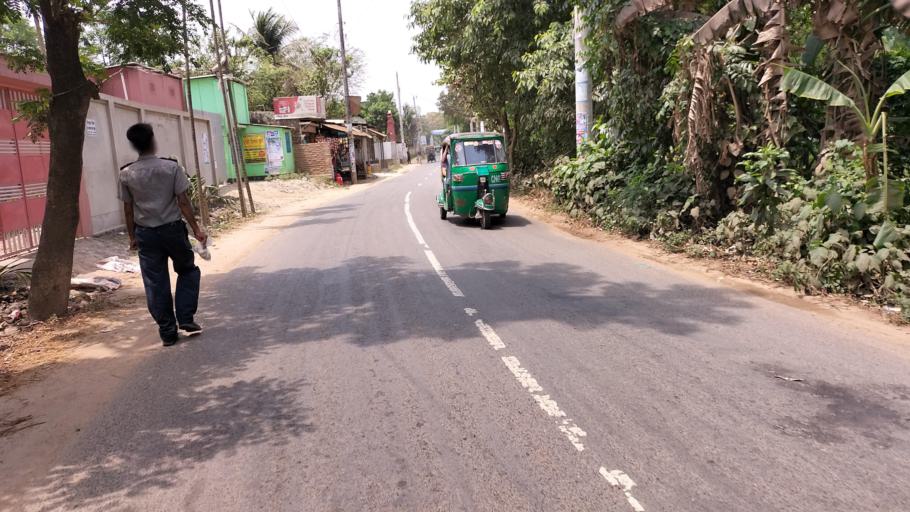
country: BD
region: Dhaka
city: Azimpur
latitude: 23.7285
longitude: 90.2958
